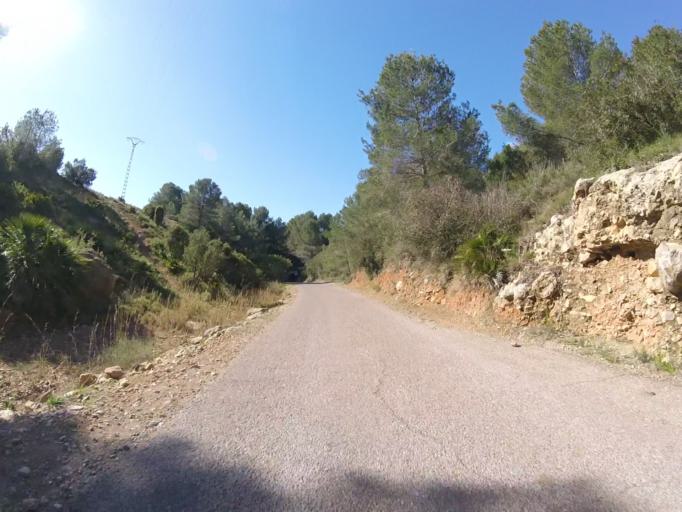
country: ES
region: Valencia
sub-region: Provincia de Castello
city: Orpesa/Oropesa del Mar
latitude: 40.0807
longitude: 0.1193
